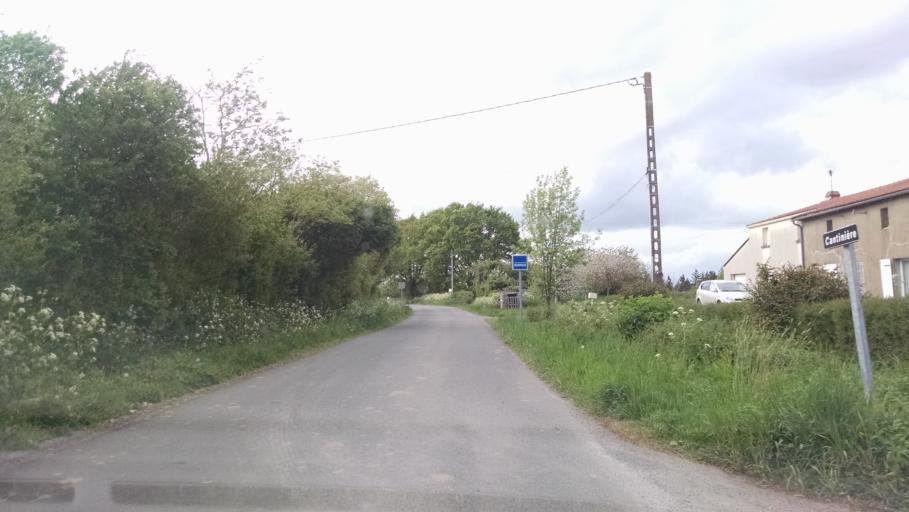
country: FR
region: Pays de la Loire
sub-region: Departement de la Vendee
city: Saint-Hilaire-de-Loulay
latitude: 46.9869
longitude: -1.3399
